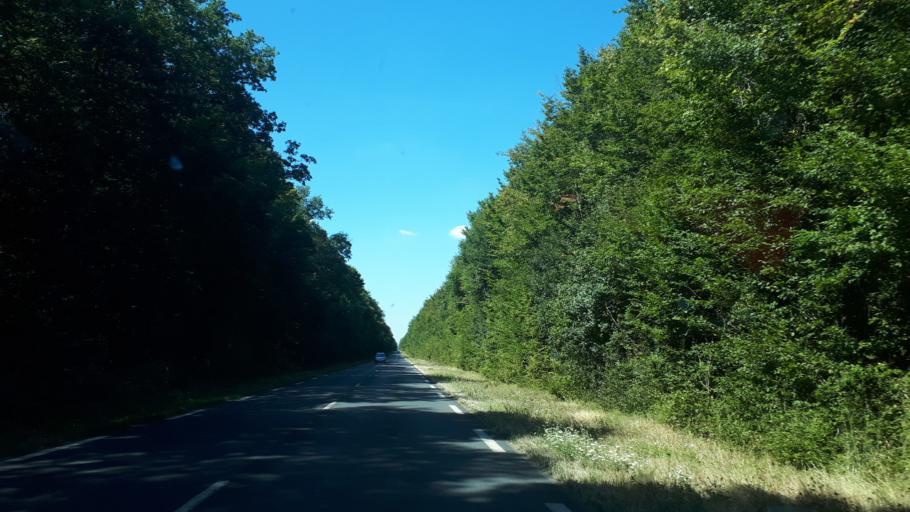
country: FR
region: Centre
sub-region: Departement du Loir-et-Cher
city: Mont-pres-Chambord
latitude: 47.5622
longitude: 1.4205
